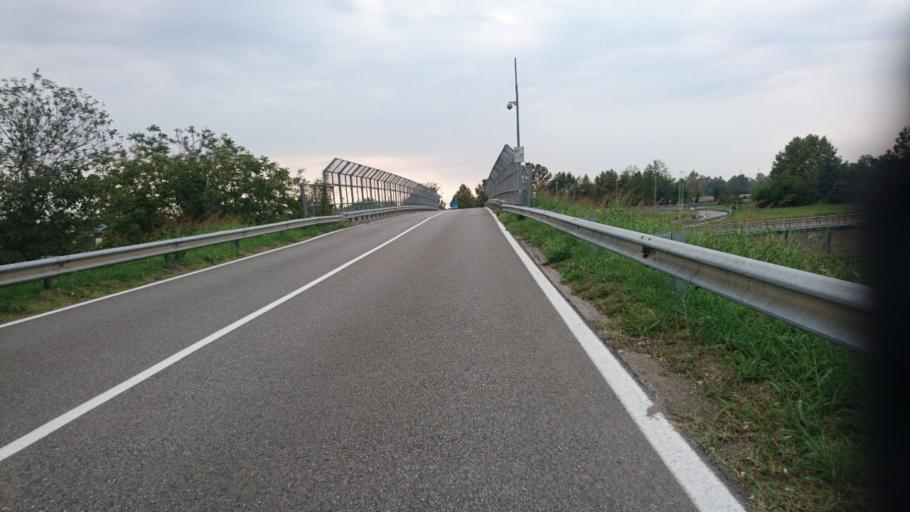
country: IT
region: Veneto
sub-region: Provincia di Verona
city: San Martino Buon Albergo
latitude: 45.4091
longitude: 11.0820
